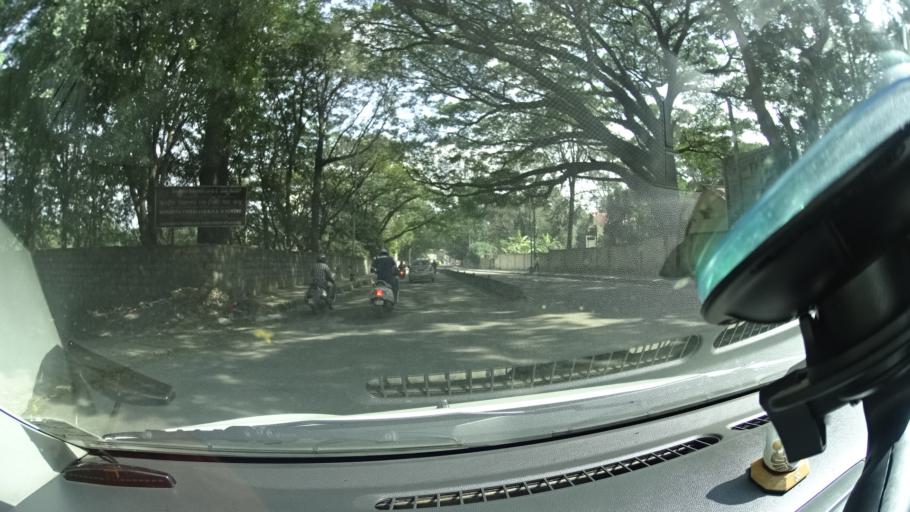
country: IN
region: Karnataka
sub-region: Bangalore Urban
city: Bangalore
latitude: 12.9896
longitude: 77.6156
